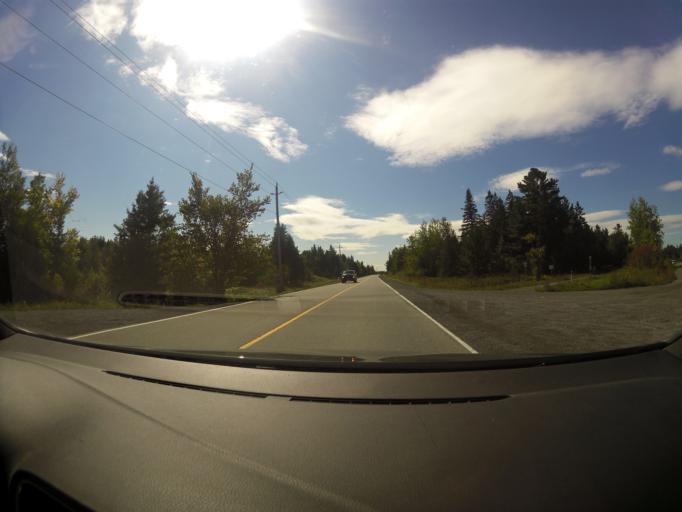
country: CA
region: Ontario
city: Bells Corners
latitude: 45.2198
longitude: -75.9821
